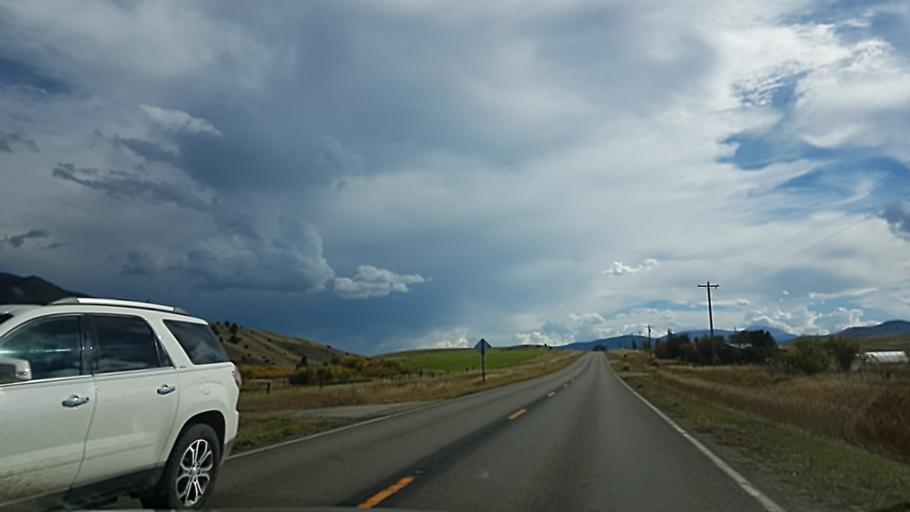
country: US
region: Montana
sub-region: Jefferson County
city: Whitehall
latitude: 45.8446
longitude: -111.9404
